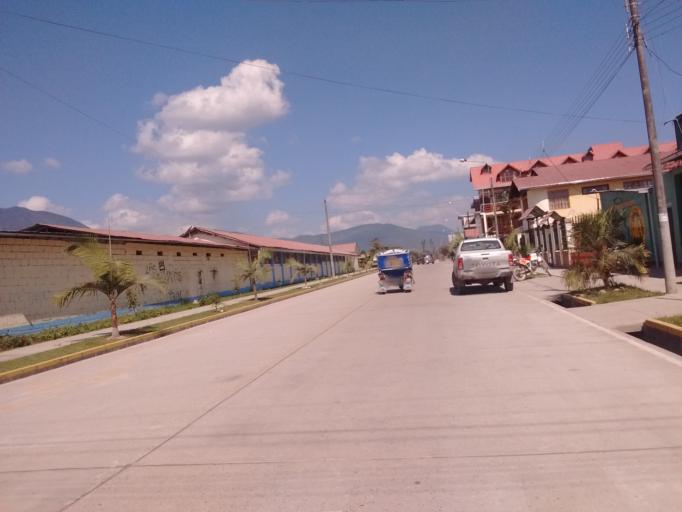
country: PE
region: Pasco
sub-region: Provincia de Oxapampa
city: Oxapampa
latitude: -10.5779
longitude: -75.4036
